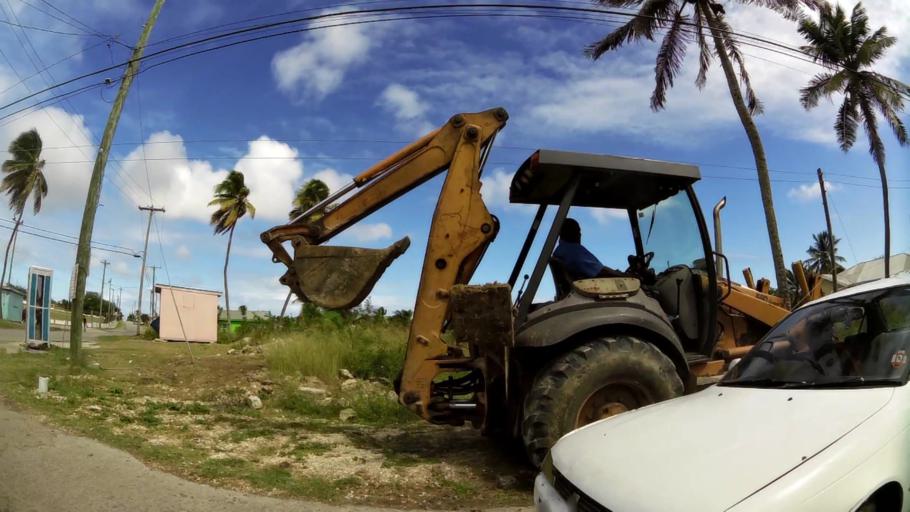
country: AG
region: Saint Paul
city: Liberta
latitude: 17.0443
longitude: -61.7510
